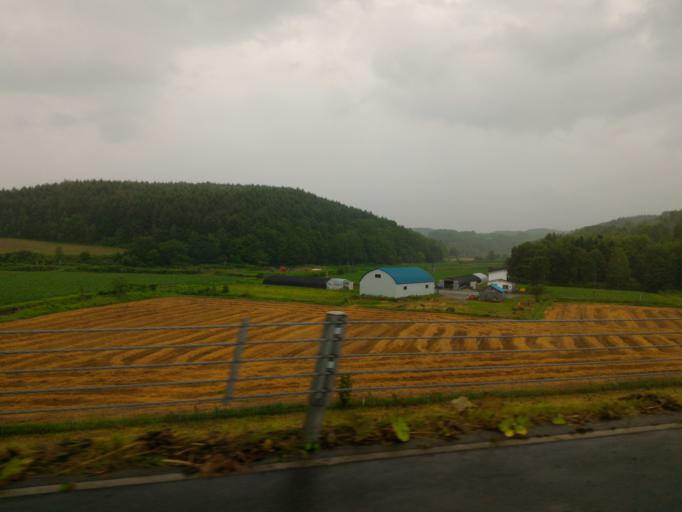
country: JP
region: Hokkaido
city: Nayoro
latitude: 44.4127
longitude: 142.4042
